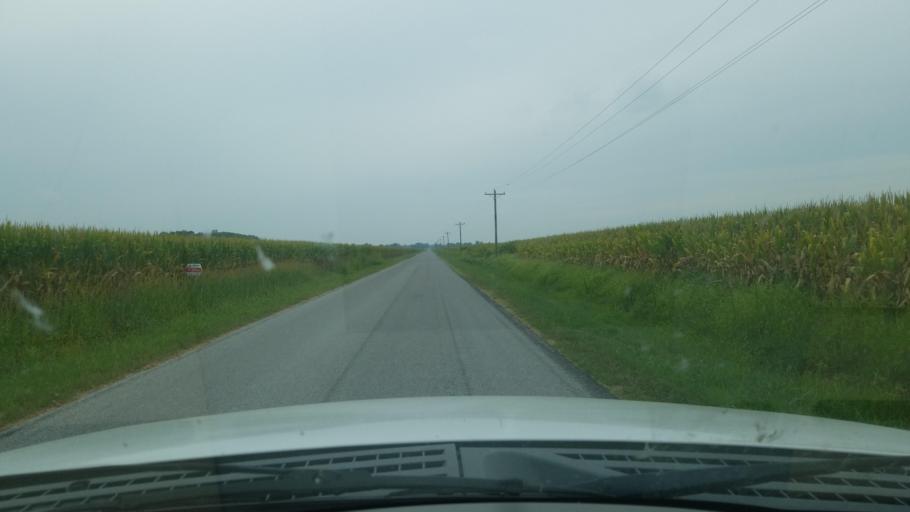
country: US
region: Illinois
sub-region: Saline County
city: Eldorado
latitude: 37.8670
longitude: -88.4608
